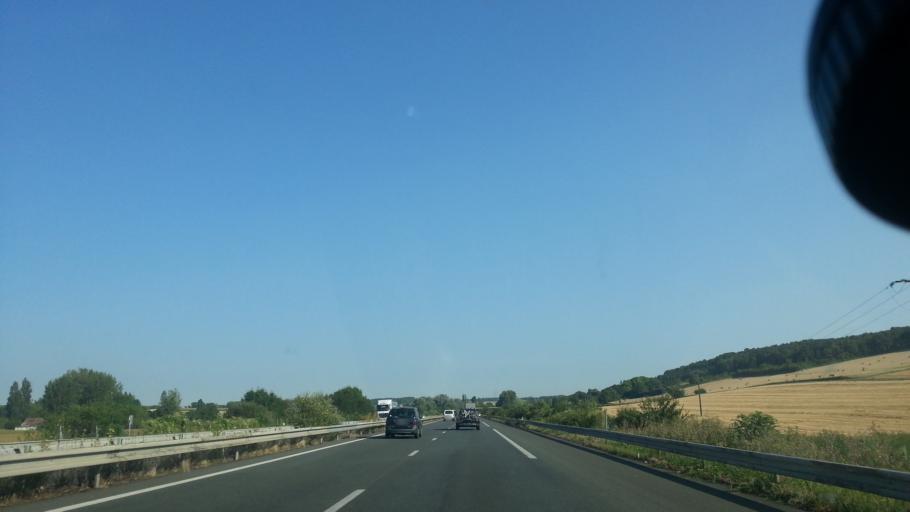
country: FR
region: Poitou-Charentes
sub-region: Departement de la Vienne
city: Antran
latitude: 46.8703
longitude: 0.5221
